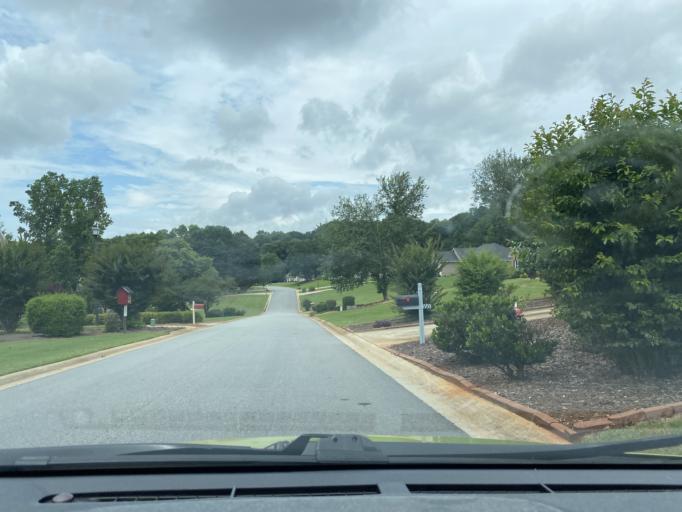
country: US
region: Georgia
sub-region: Fulton County
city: Palmetto
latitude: 33.4281
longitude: -84.6835
